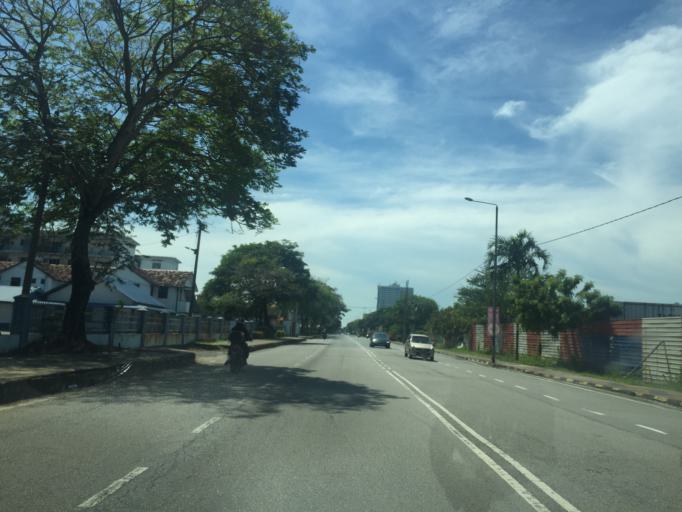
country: MY
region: Penang
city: Butterworth
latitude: 5.4046
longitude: 100.3691
